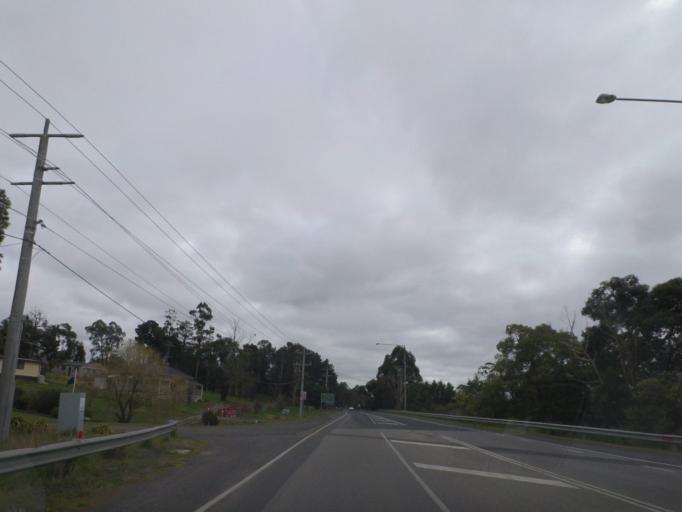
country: AU
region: Victoria
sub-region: Whittlesea
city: Whittlesea
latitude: -37.3538
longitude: 145.0254
